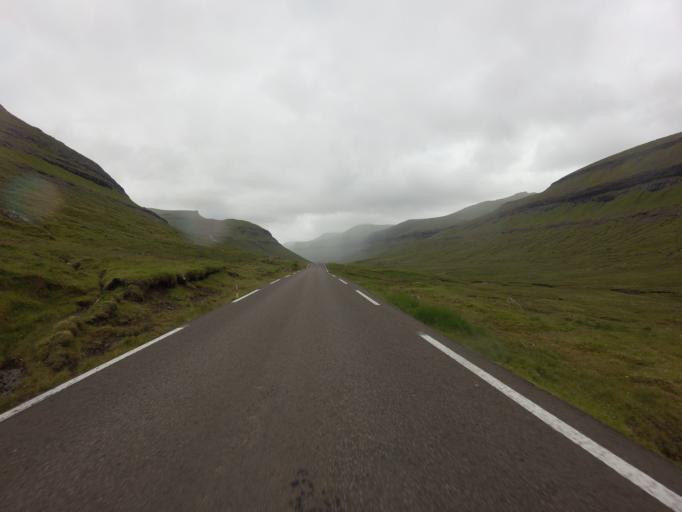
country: FO
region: Streymoy
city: Vestmanna
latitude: 62.2146
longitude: -7.1164
